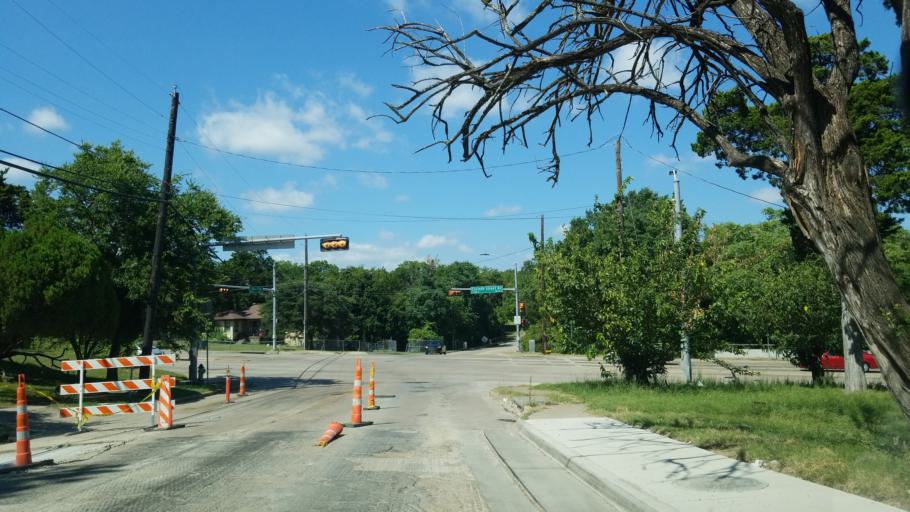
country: US
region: Texas
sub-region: Dallas County
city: Dallas
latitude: 32.7290
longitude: -96.7985
